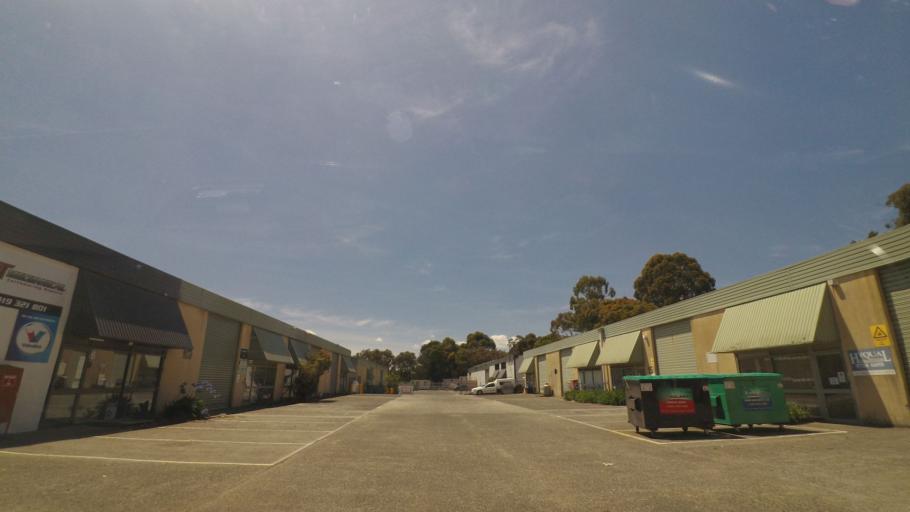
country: AU
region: Victoria
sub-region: Maroondah
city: Kilsyth South
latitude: -37.8150
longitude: 145.3225
